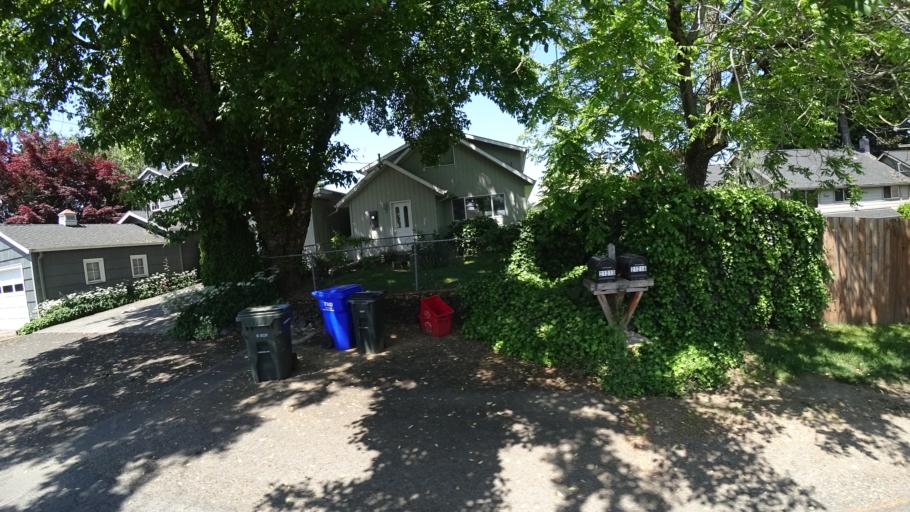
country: US
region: Oregon
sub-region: Multnomah County
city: Fairview
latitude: 45.5521
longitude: -122.4446
